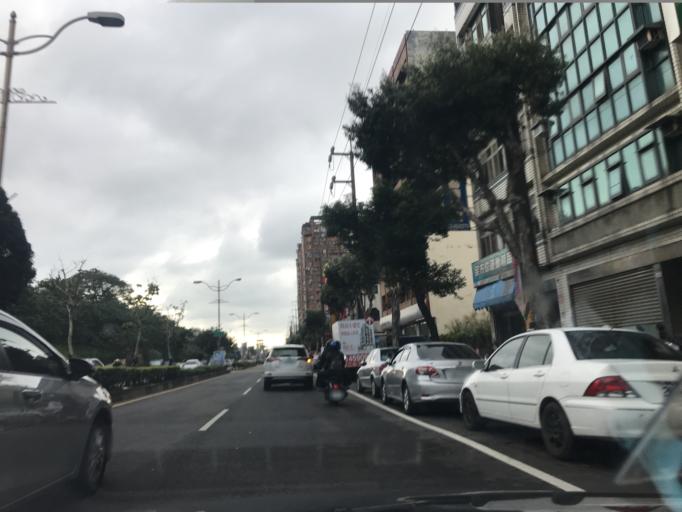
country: TW
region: Taiwan
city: Taoyuan City
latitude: 24.9497
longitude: 121.2375
